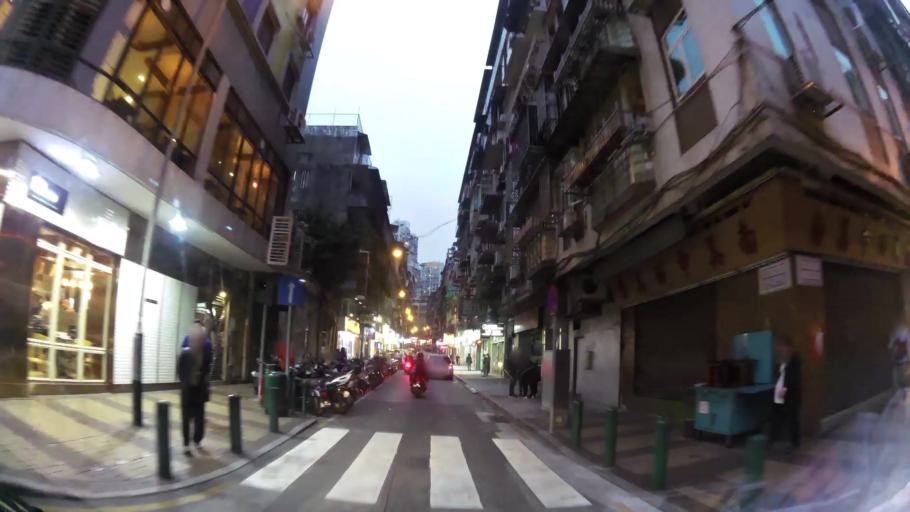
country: MO
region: Macau
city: Macau
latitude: 22.2018
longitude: 113.5455
